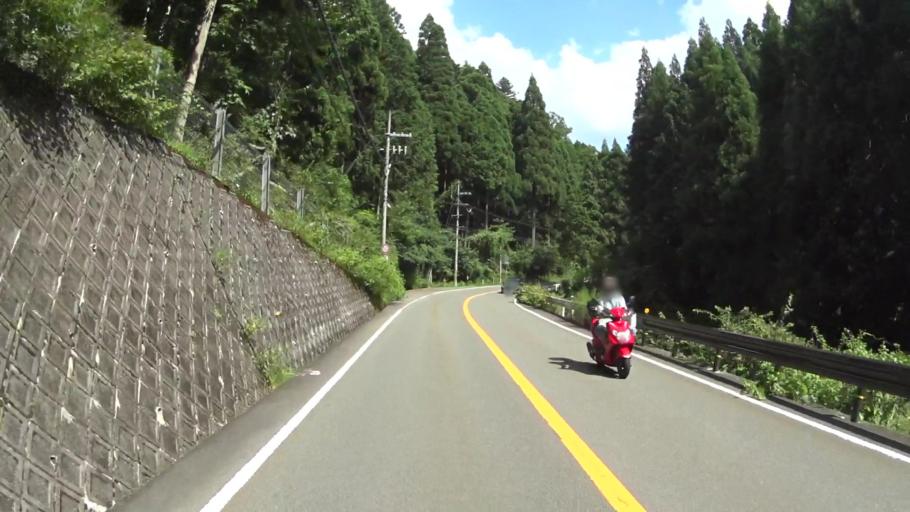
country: JP
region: Kyoto
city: Kameoka
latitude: 35.2670
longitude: 135.5961
